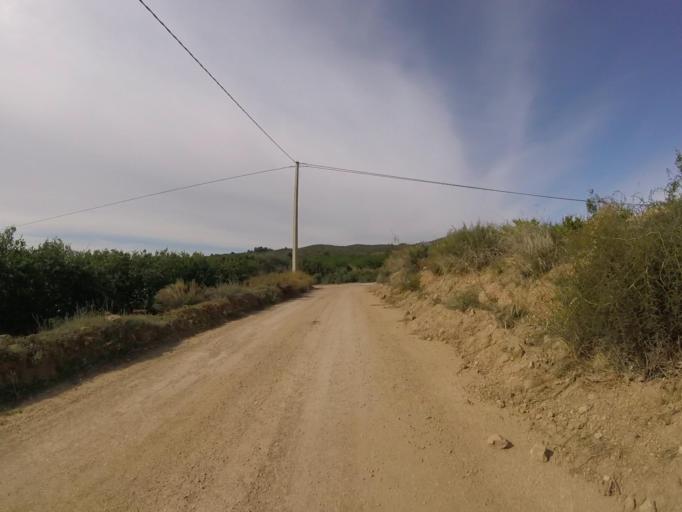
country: ES
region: Valencia
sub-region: Provincia de Castello
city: Torreblanca
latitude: 40.1955
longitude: 0.1608
